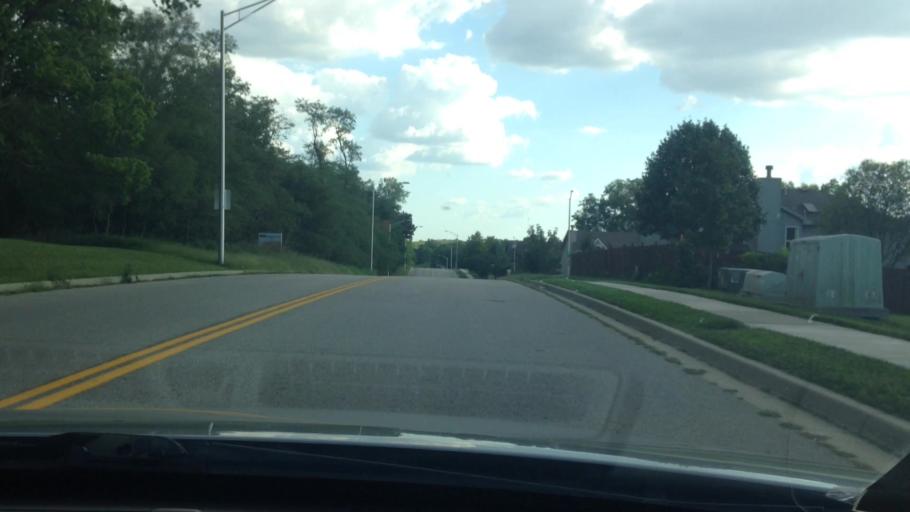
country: US
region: Missouri
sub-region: Clay County
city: Claycomo
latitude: 39.1756
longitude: -94.5029
